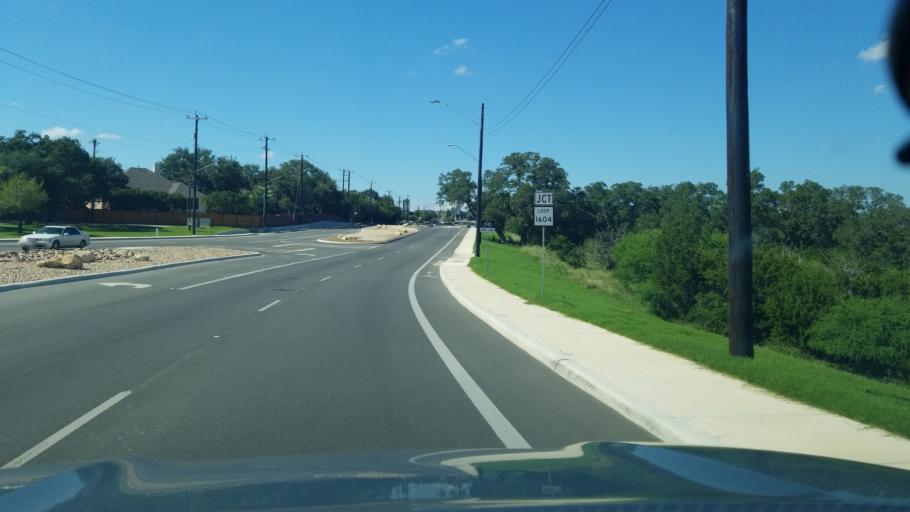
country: US
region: Texas
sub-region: Bexar County
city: Hollywood Park
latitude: 29.5988
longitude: -98.4406
